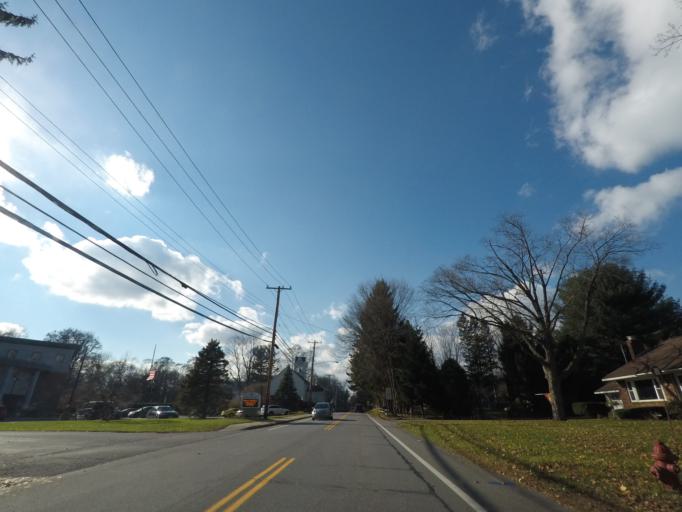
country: US
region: New York
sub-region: Schenectady County
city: East Glenville
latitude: 42.9102
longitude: -73.8903
